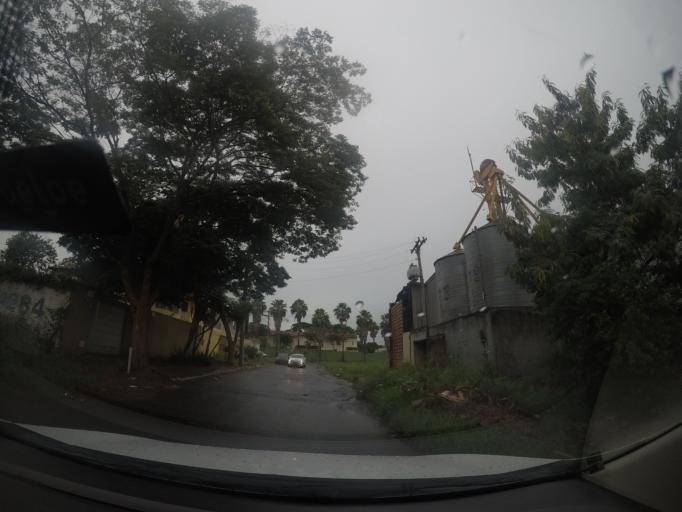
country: BR
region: Goias
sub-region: Goiania
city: Goiania
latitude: -16.6366
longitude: -49.2361
